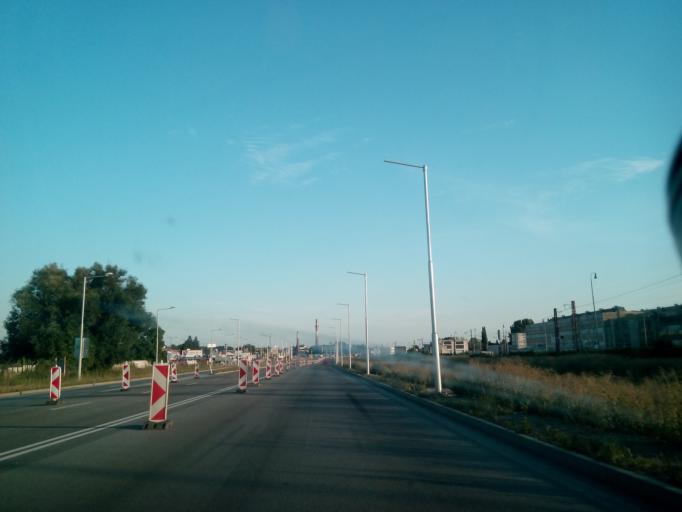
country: SK
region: Presovsky
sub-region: Okres Presov
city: Presov
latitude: 48.9755
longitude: 21.2520
